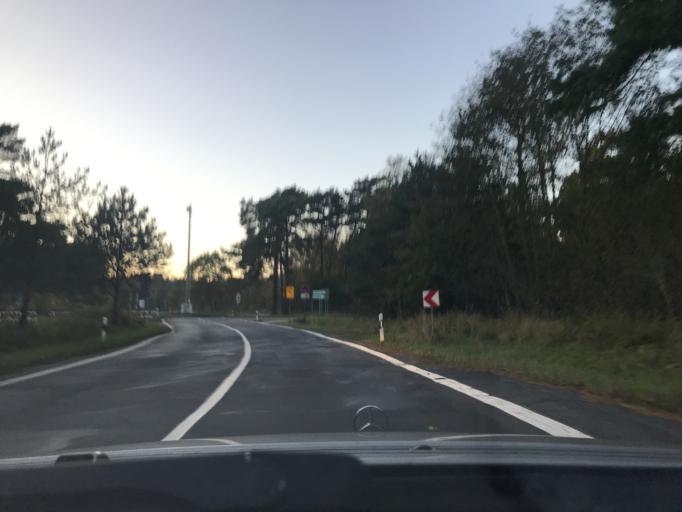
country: DE
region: Mecklenburg-Vorpommern
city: Karlshagen
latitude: 54.1441
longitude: 13.8105
